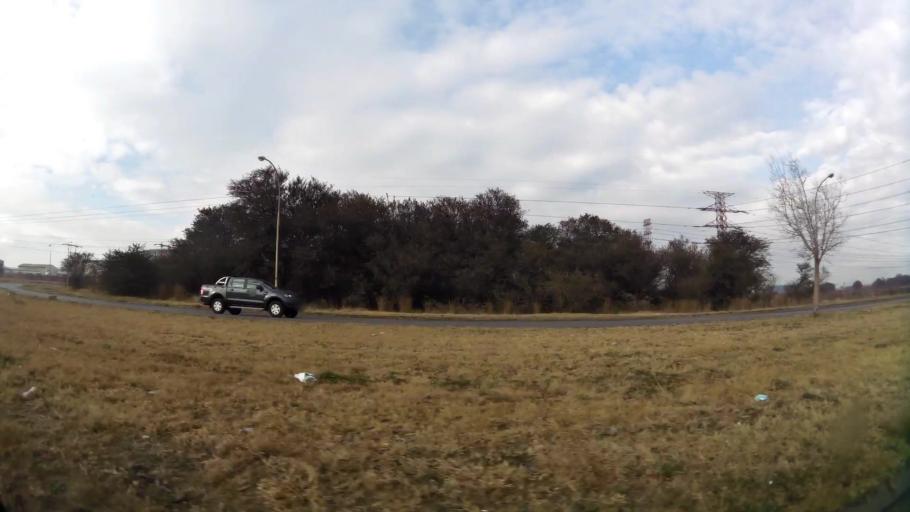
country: ZA
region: Gauteng
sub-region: Sedibeng District Municipality
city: Vanderbijlpark
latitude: -26.6727
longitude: 27.8100
